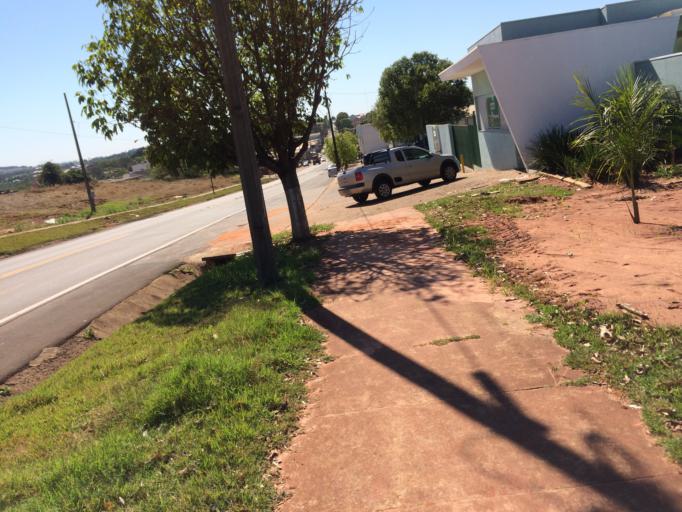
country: BR
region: Parana
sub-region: Cianorte
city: Cianorte
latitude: -23.5385
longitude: -52.5978
